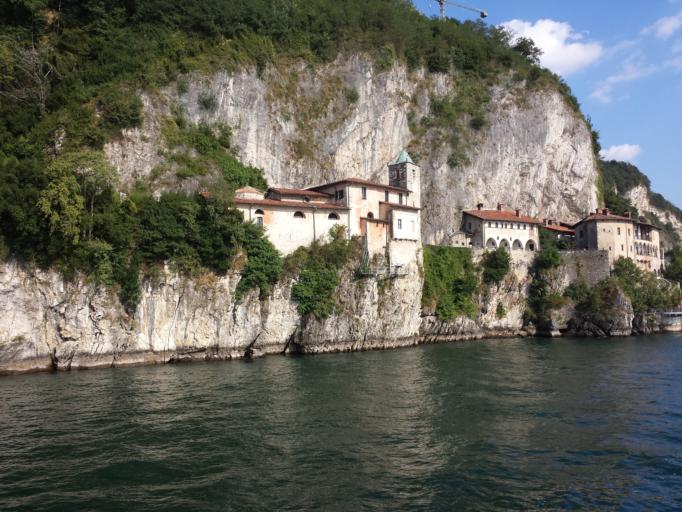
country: IT
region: Lombardy
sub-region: Provincia di Varese
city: Leggiuno
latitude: 45.8777
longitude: 8.5957
